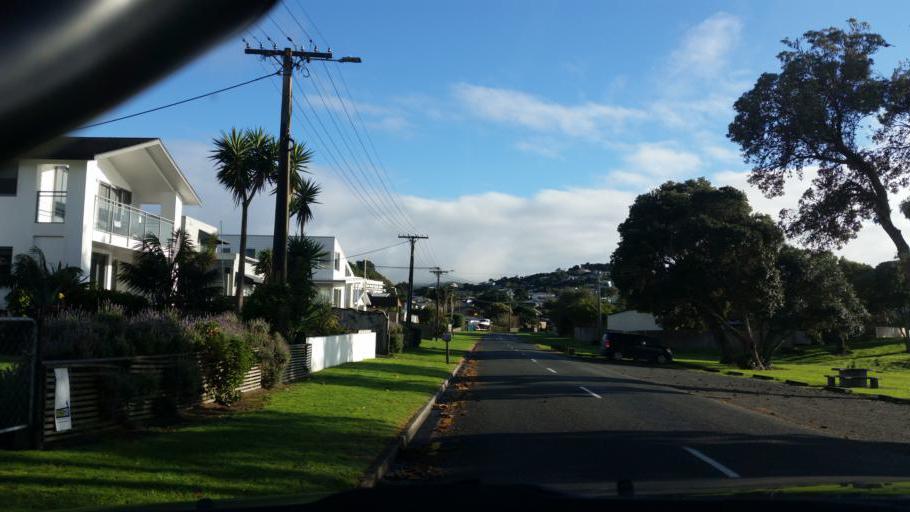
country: NZ
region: Auckland
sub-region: Auckland
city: Wellsford
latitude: -36.0897
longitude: 174.5896
